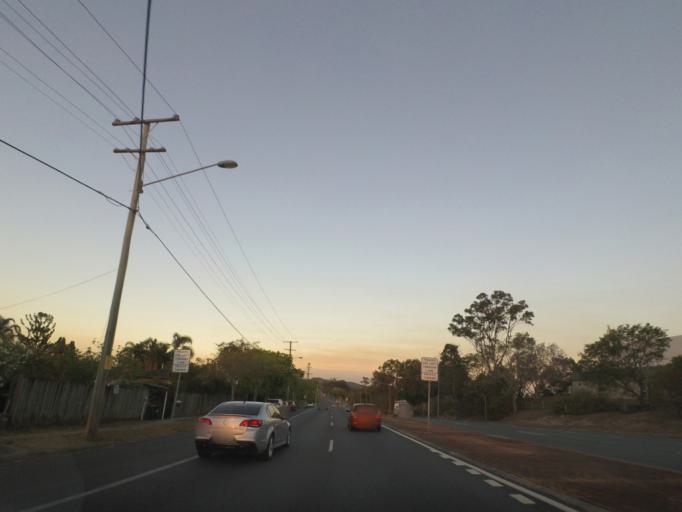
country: AU
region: Queensland
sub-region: Brisbane
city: Mansfield
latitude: -27.5545
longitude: 153.0998
